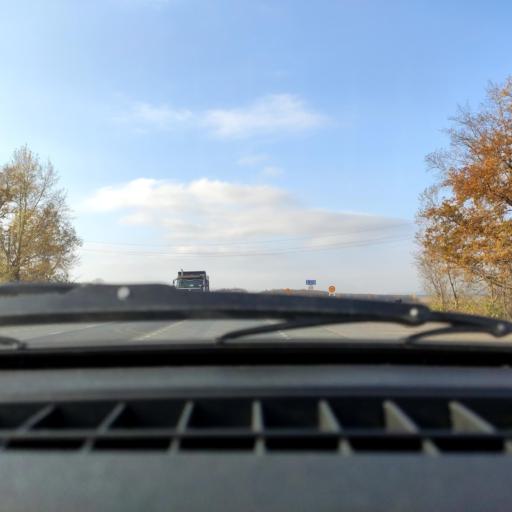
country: RU
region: Bashkortostan
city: Iglino
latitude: 54.7291
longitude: 56.2553
